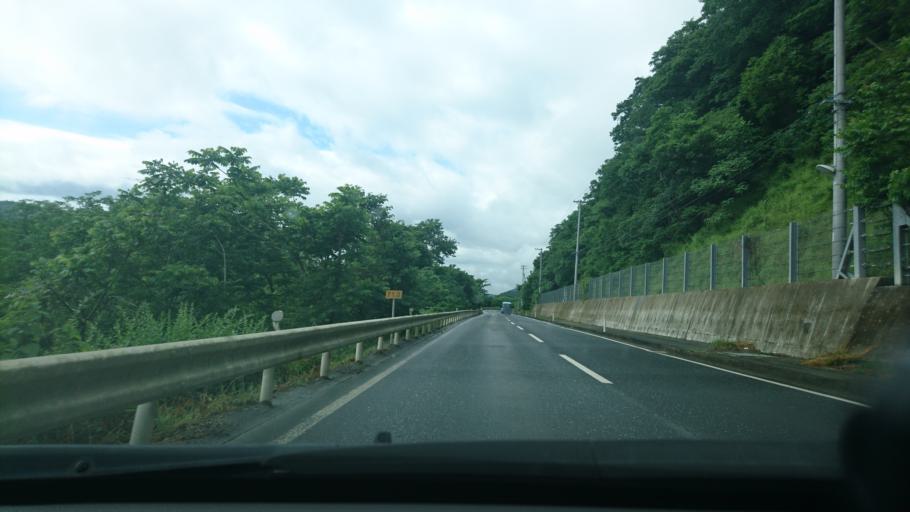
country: JP
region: Miyagi
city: Ishinomaki
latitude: 38.5851
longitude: 141.3041
